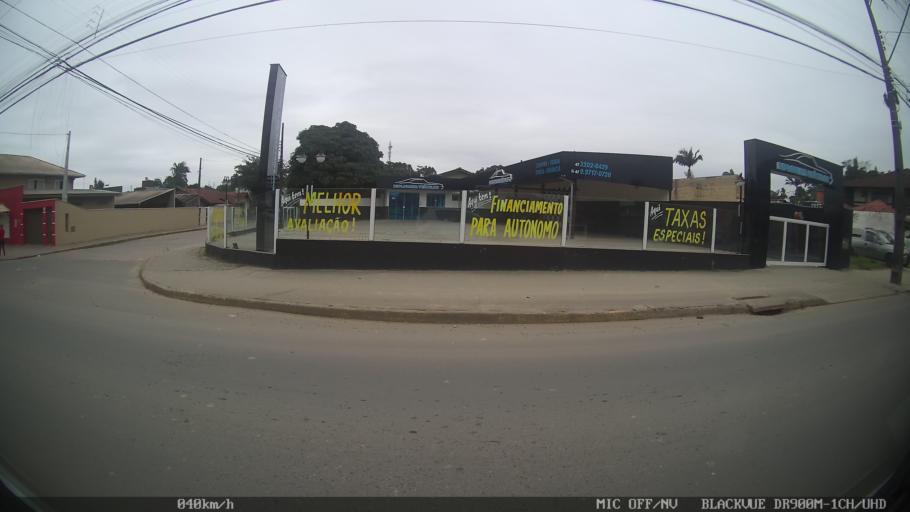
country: BR
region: Santa Catarina
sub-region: Joinville
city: Joinville
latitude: -26.3396
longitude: -48.8103
